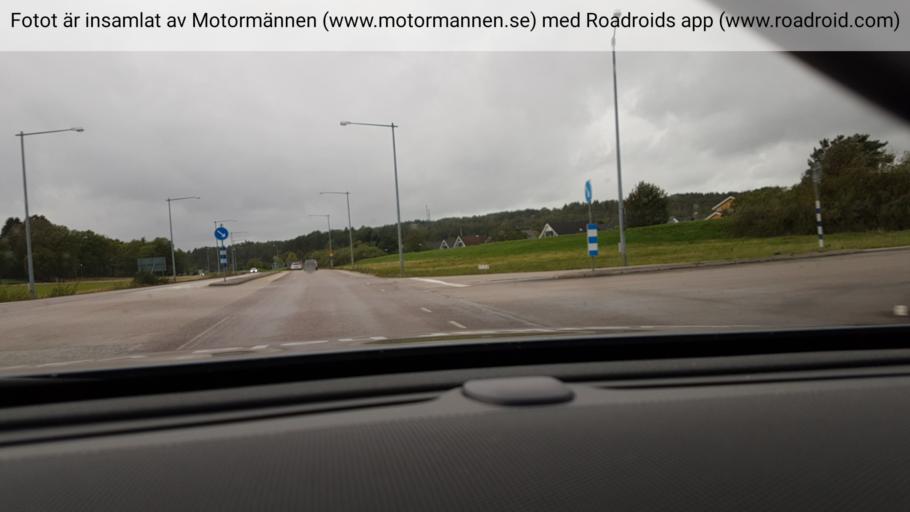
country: SE
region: Vaestra Goetaland
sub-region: Stenungsunds Kommun
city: Stora Hoga
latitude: 58.0520
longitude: 11.8599
